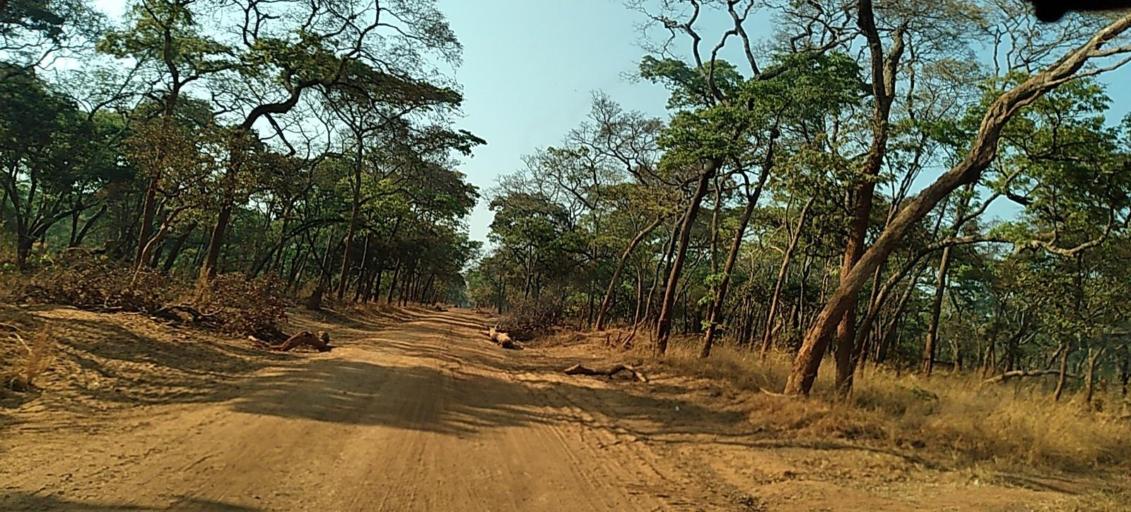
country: ZM
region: North-Western
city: Kasempa
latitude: -13.5512
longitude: 25.9968
